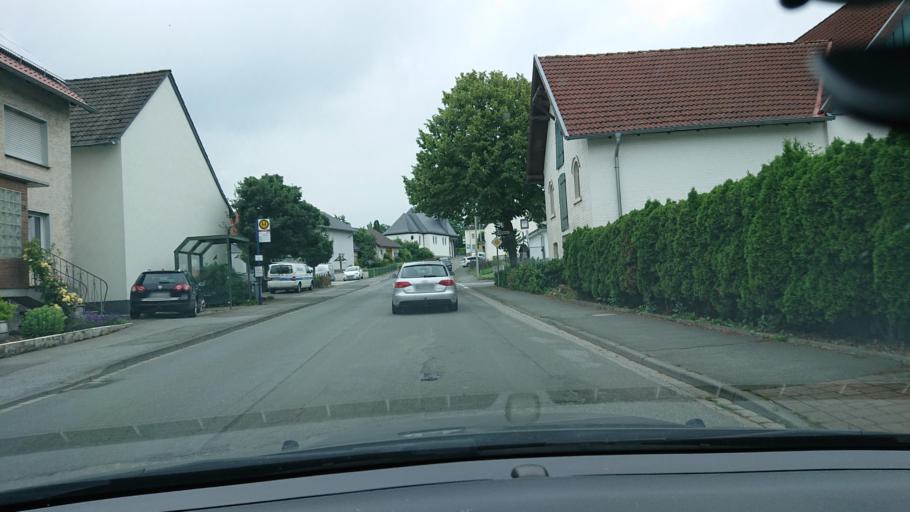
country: DE
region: North Rhine-Westphalia
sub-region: Regierungsbezirk Arnsberg
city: Mohnesee
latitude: 51.4786
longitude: 8.2241
